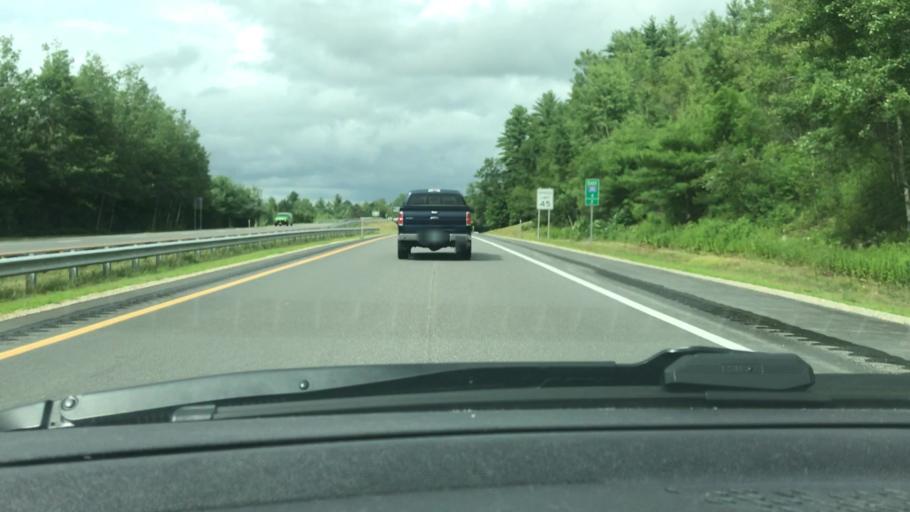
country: US
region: New Hampshire
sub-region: Merrimack County
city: Chichester
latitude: 43.2386
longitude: -71.4588
